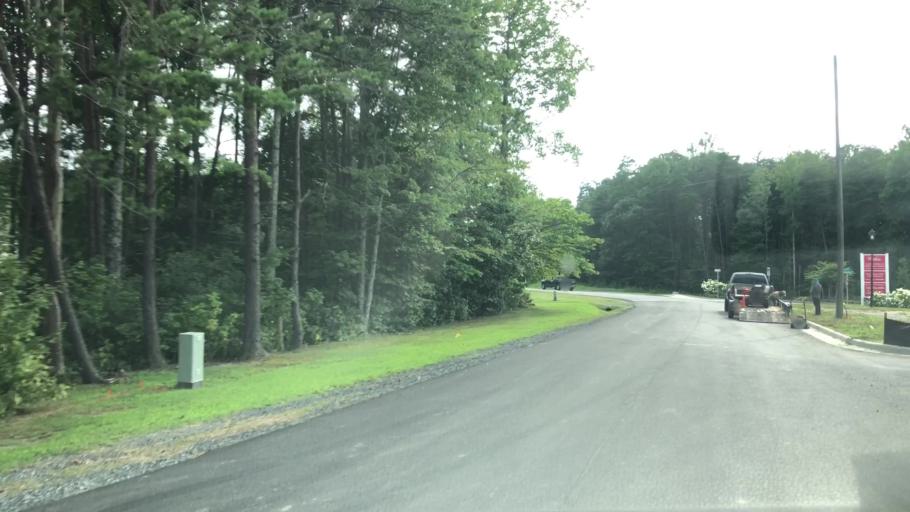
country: US
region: Virginia
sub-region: Stafford County
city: Stafford
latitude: 38.4240
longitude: -77.4640
